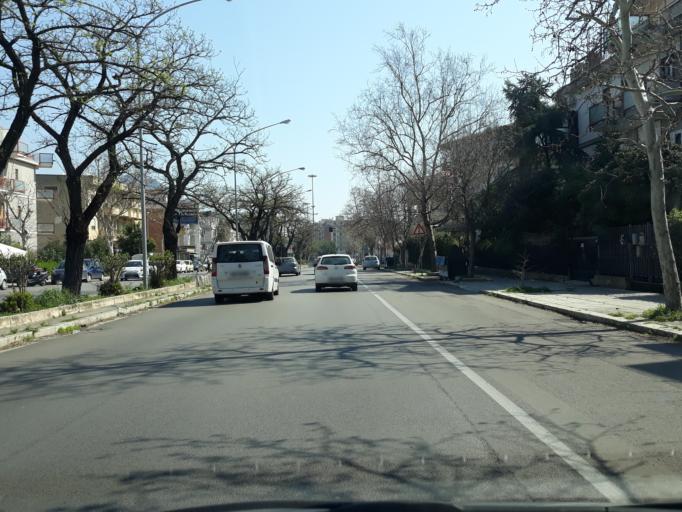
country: IT
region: Sicily
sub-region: Palermo
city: Palermo
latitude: 38.1388
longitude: 13.3272
